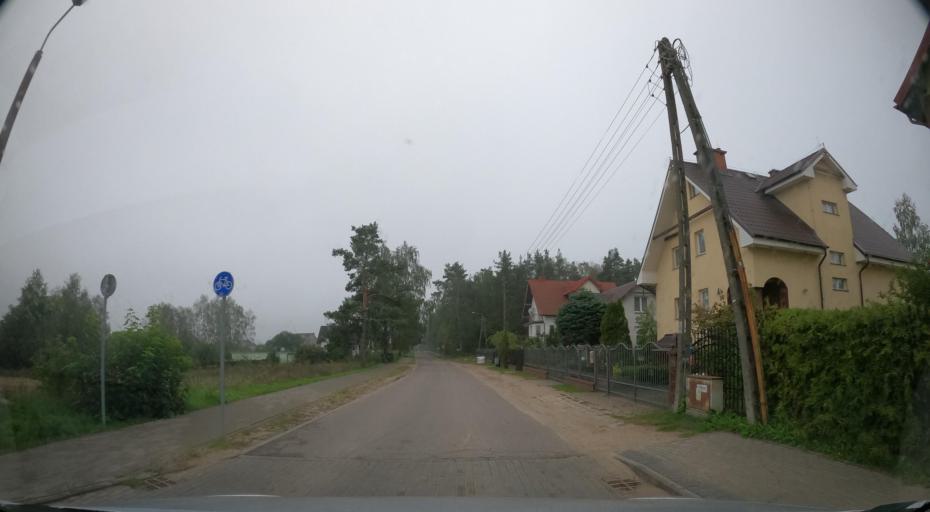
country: PL
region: Pomeranian Voivodeship
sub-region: Powiat kartuski
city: Chwaszczyno
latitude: 54.4390
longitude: 18.4183
